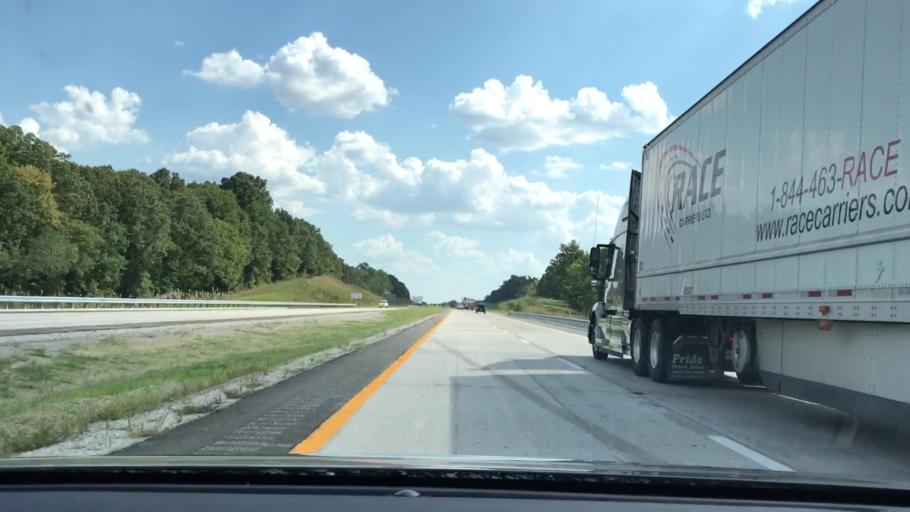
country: US
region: Kentucky
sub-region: Ohio County
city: Oak Grove
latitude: 37.3778
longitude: -86.8052
